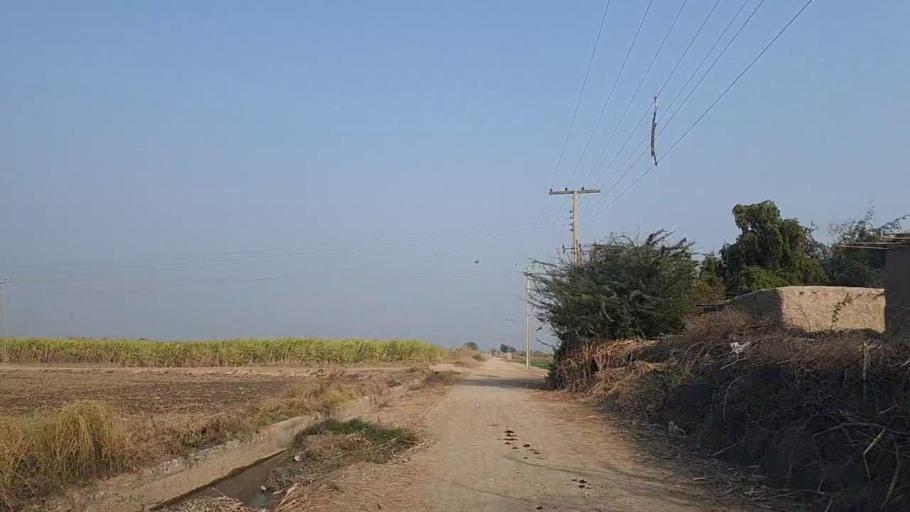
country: PK
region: Sindh
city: Sann
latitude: 26.1122
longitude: 68.1667
